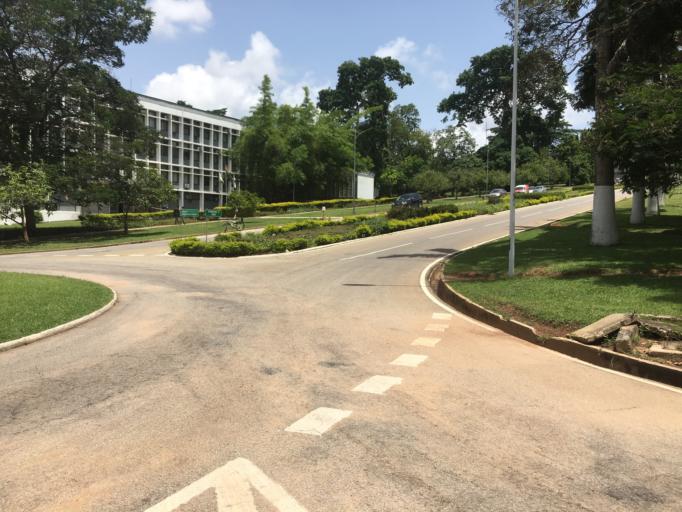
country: GH
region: Ashanti
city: Kumasi
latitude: 6.6753
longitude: -1.5709
